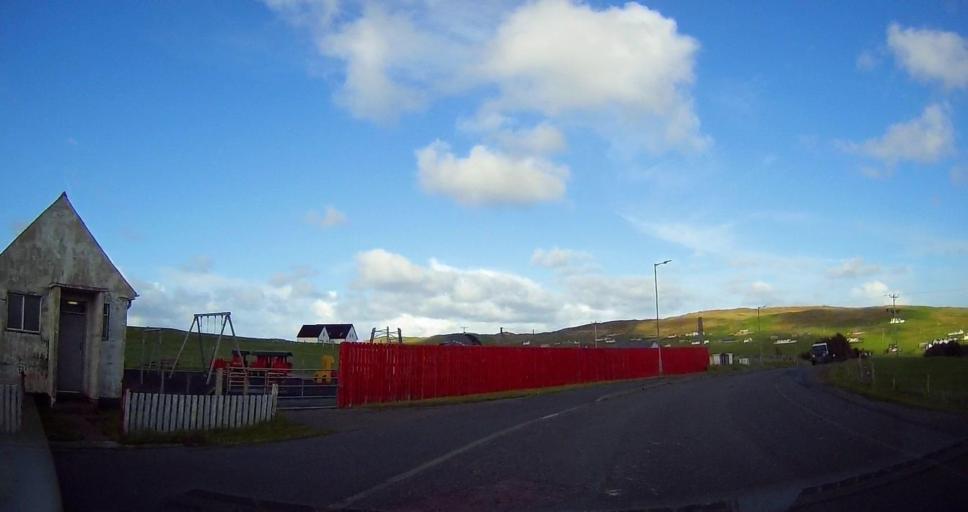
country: GB
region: Scotland
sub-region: Shetland Islands
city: Shetland
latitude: 60.3690
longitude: -1.1400
